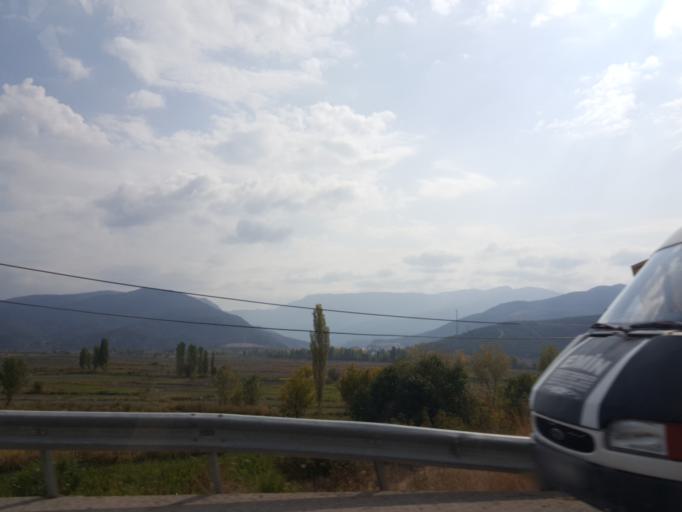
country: TR
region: Corum
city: Hacihamza
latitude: 41.1131
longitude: 34.3975
